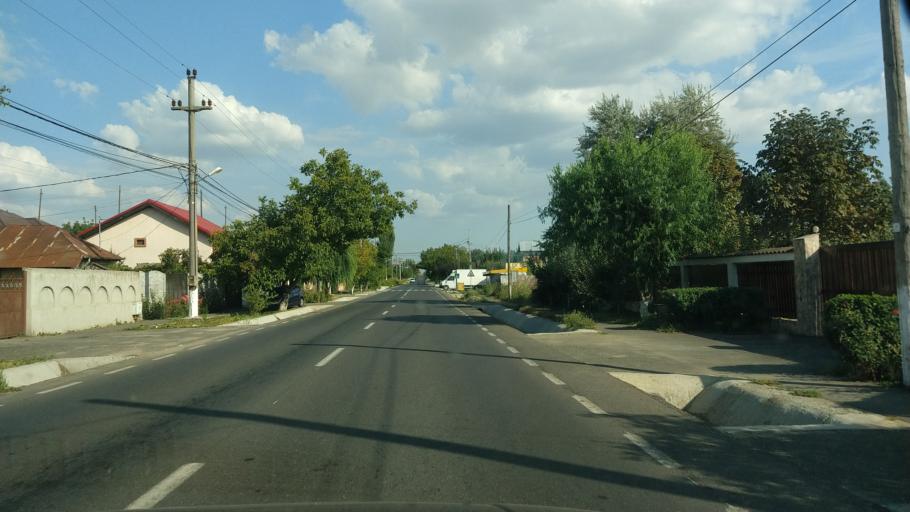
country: RO
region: Ilfov
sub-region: Comuna Afumati
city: Afumati
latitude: 44.5306
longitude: 26.2360
